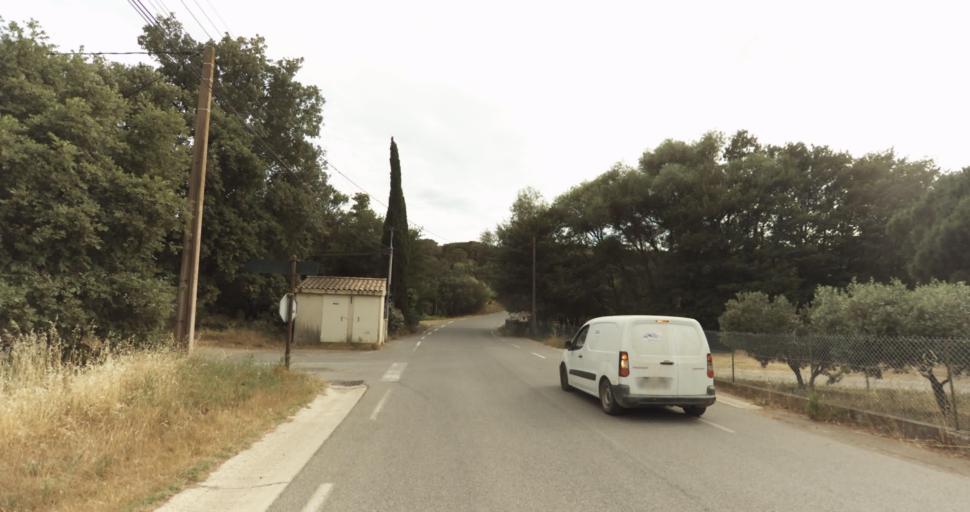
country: FR
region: Provence-Alpes-Cote d'Azur
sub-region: Departement du Var
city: Gassin
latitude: 43.2147
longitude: 6.5803
